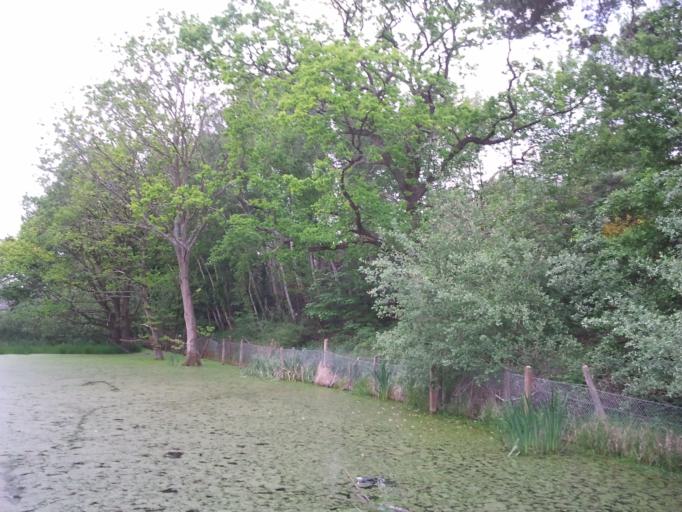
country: GB
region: England
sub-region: Surrey
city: Bagshot
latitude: 51.3582
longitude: -0.6913
